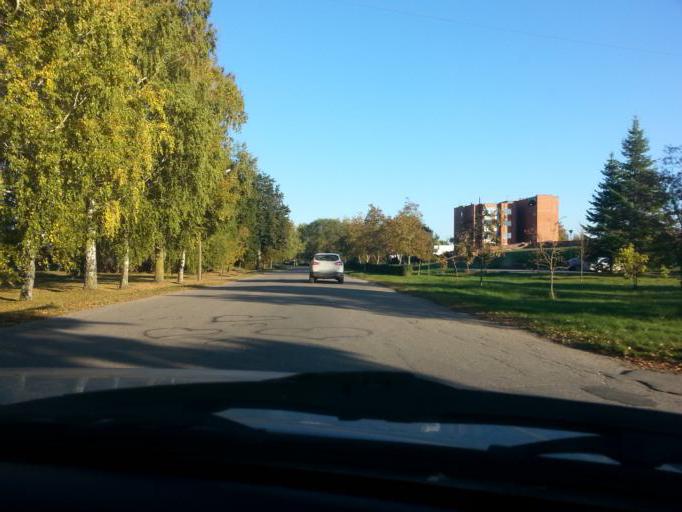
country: LV
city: Tervete
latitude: 56.6196
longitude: 23.4360
